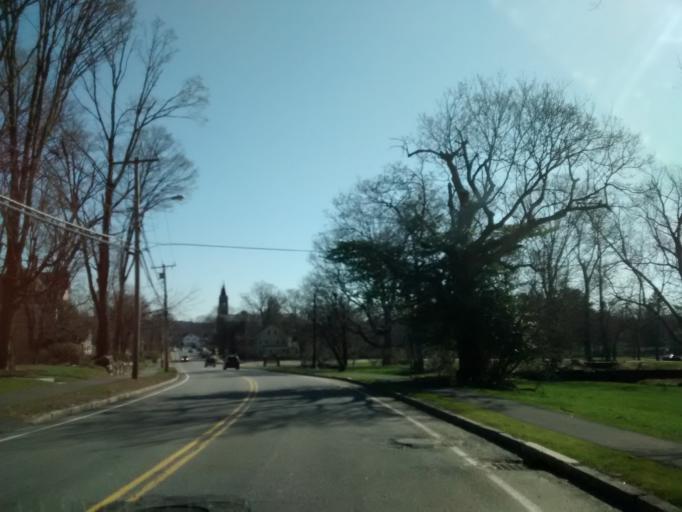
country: US
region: Massachusetts
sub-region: Worcester County
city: Westborough
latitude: 42.2650
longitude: -71.6198
